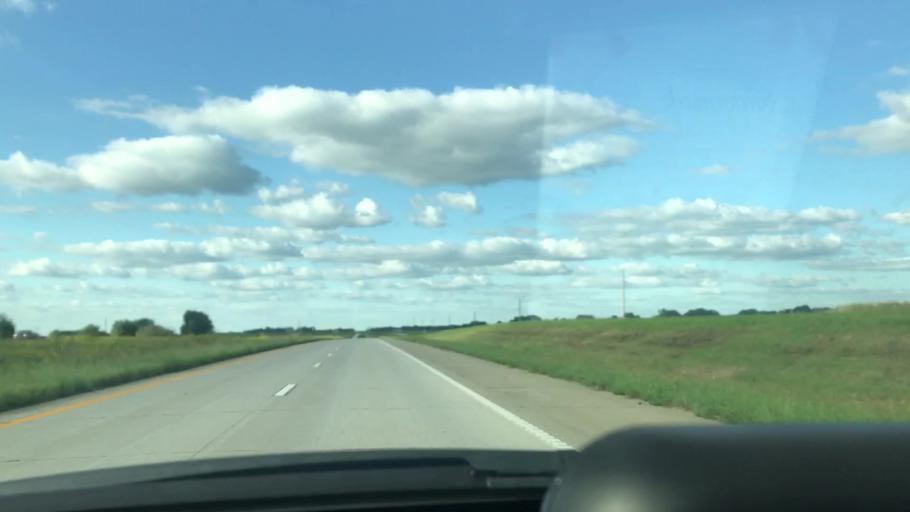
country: US
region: Missouri
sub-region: Benton County
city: Cole Camp
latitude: 38.5079
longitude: -93.2728
